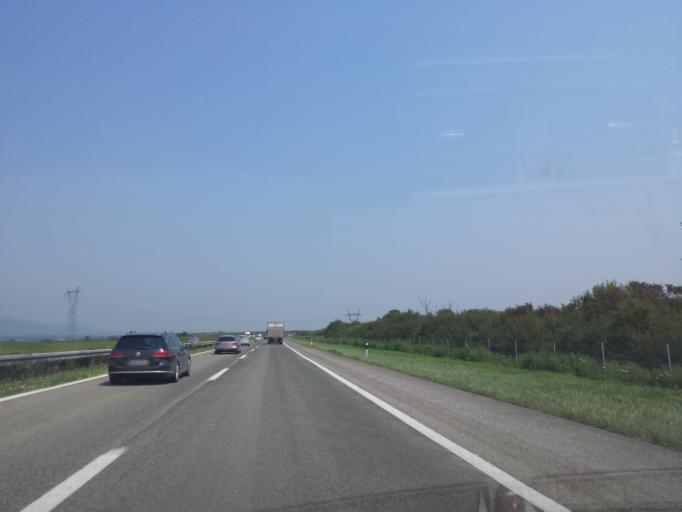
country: HR
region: Zagrebacka
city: Jastrebarsko
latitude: 45.6204
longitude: 15.6499
